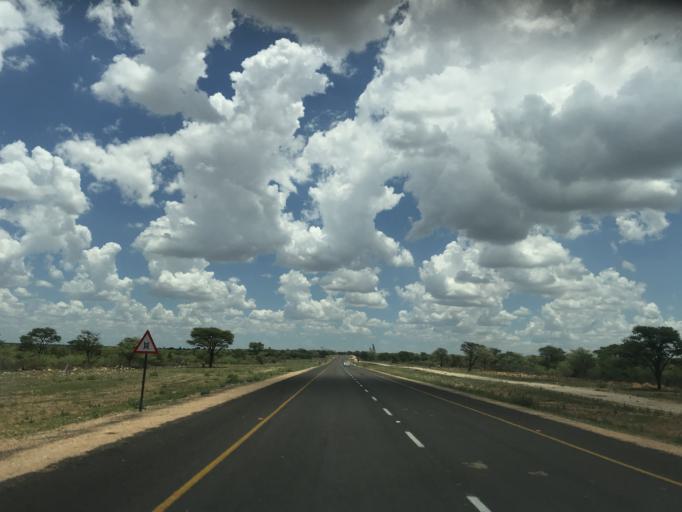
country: BW
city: Mabuli
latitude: -25.8035
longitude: 24.8304
